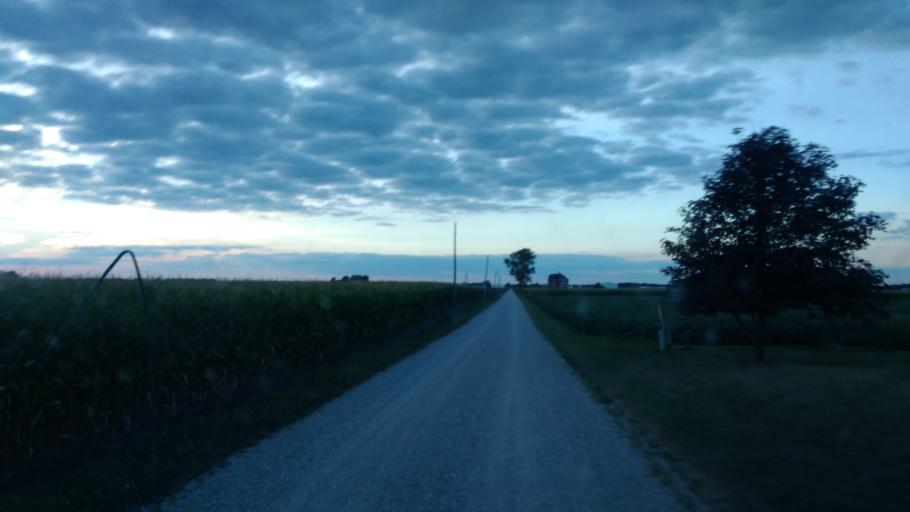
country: US
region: Indiana
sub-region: Adams County
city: Berne
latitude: 40.6428
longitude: -85.0796
